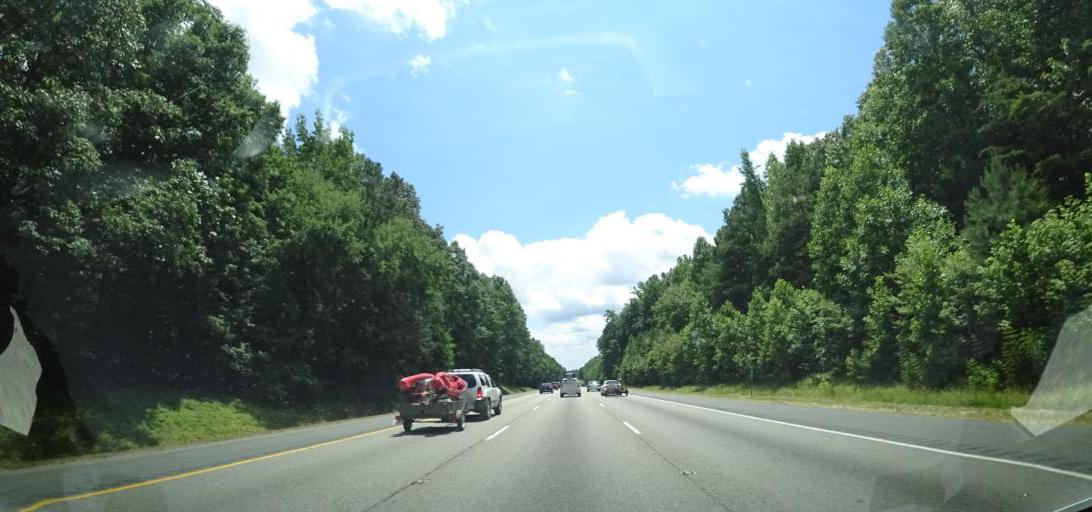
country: US
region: Virginia
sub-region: Hanover County
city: Ashland
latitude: 37.9089
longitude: -77.4595
